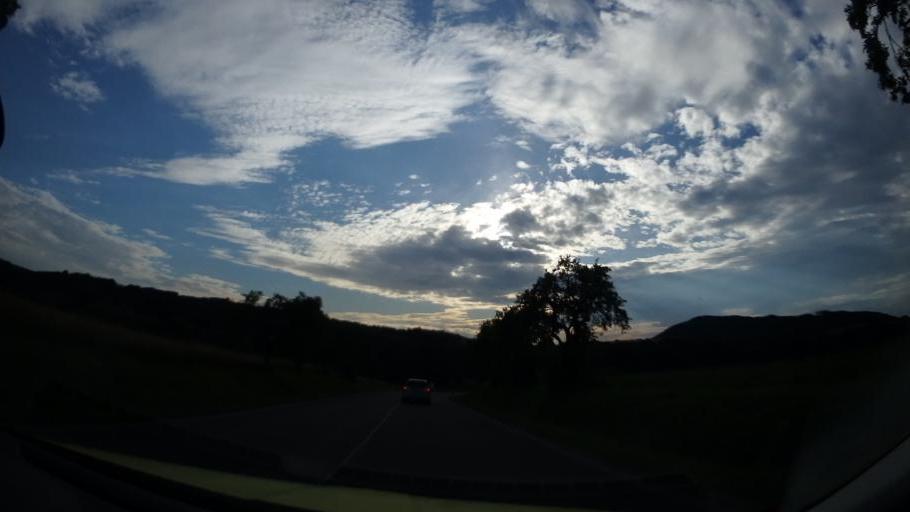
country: CZ
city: Stramberk
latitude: 49.5940
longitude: 18.1037
